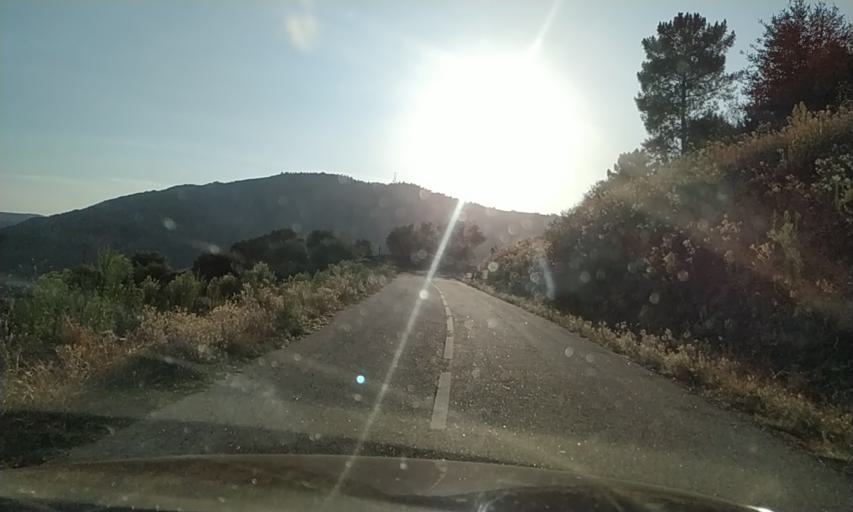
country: PT
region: Vila Real
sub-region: Sabrosa
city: Vilela
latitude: 41.1732
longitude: -7.6419
